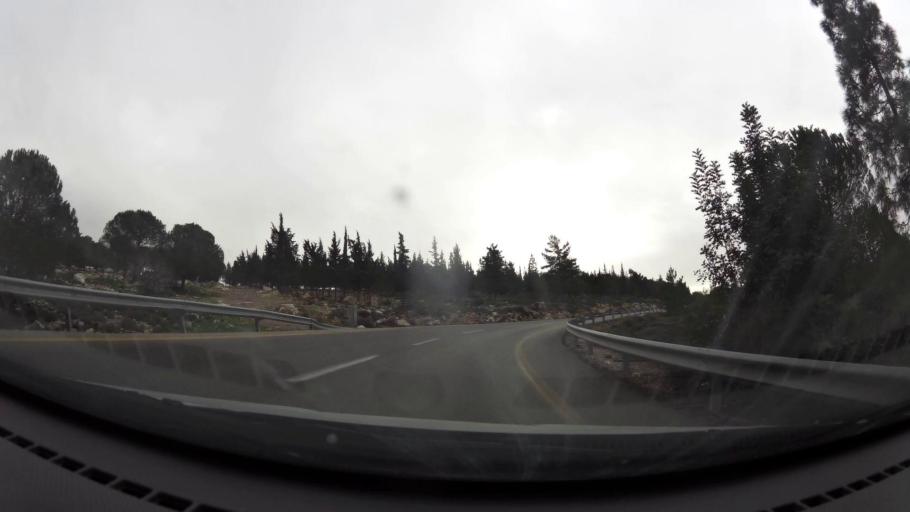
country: PS
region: West Bank
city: Nahhalin
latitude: 31.6710
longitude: 35.1062
